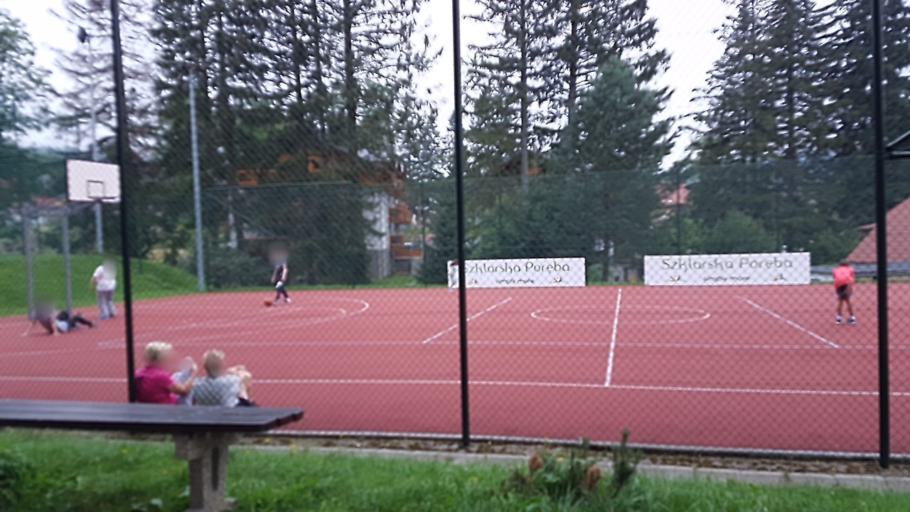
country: PL
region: Lower Silesian Voivodeship
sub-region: Powiat jeleniogorski
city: Szklarska Poreba
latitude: 50.8218
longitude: 15.5298
